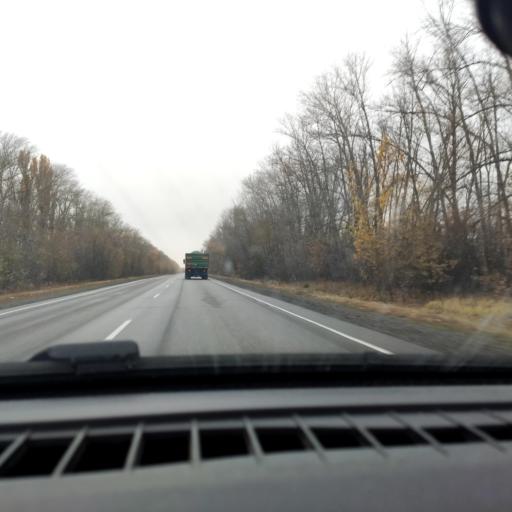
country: RU
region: Voronezj
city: Ostrogozhsk
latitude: 50.9621
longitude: 39.0213
